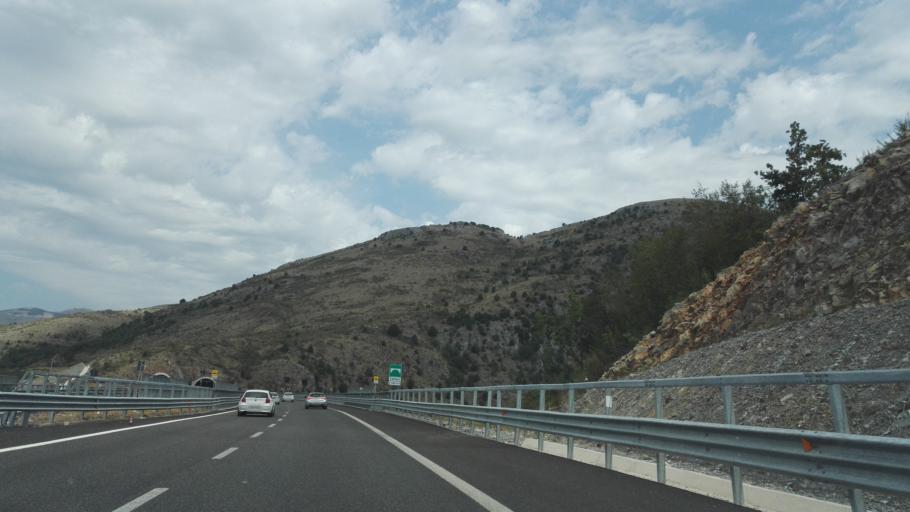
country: IT
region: Basilicate
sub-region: Provincia di Potenza
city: Lauria
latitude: 40.0333
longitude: 15.8745
